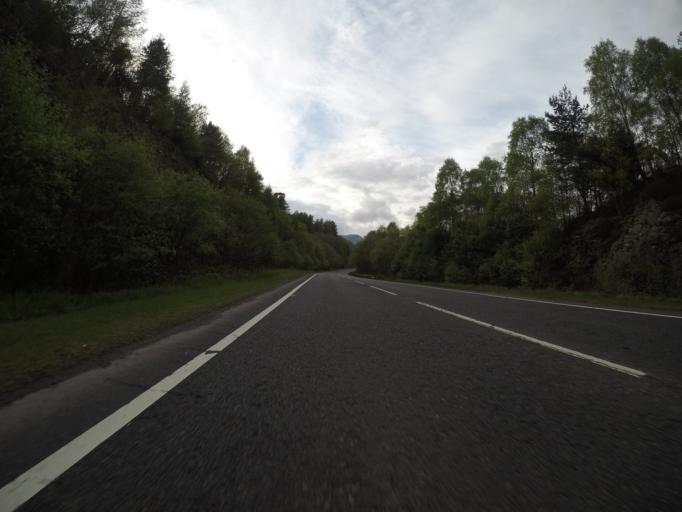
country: GB
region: Scotland
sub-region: Argyll and Bute
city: Garelochhead
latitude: 56.1789
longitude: -4.6872
